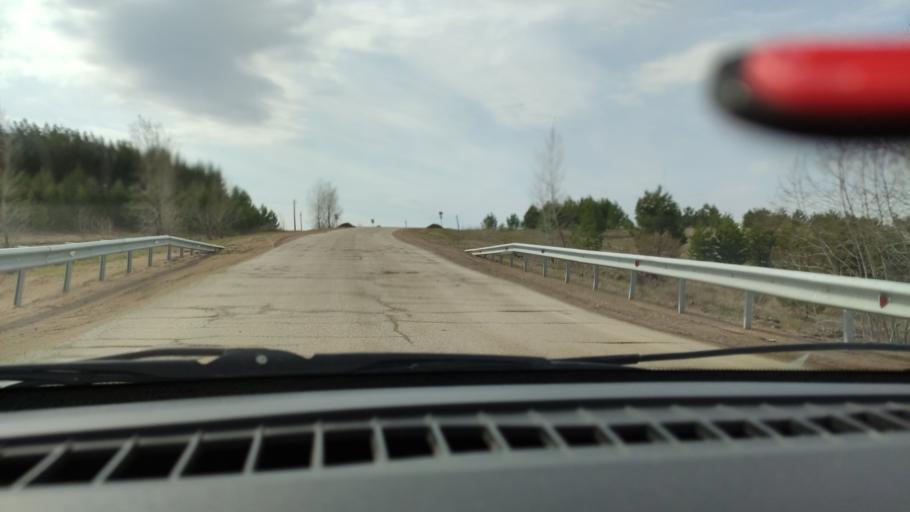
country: RU
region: Bashkortostan
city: Dyurtyuli
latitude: 55.6113
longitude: 54.9638
